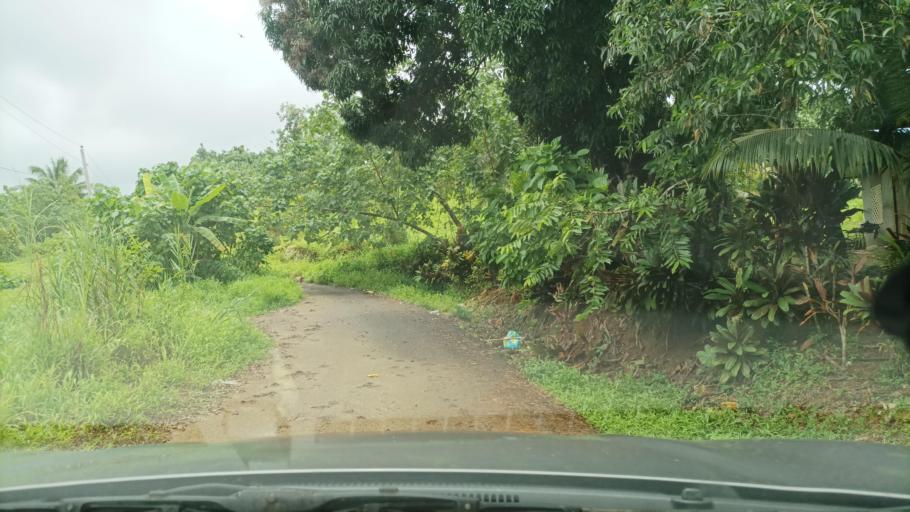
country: FM
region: Pohnpei
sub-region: Madolenihm Municipality
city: Madolenihm Municipality Government
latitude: 6.8900
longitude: 158.2915
